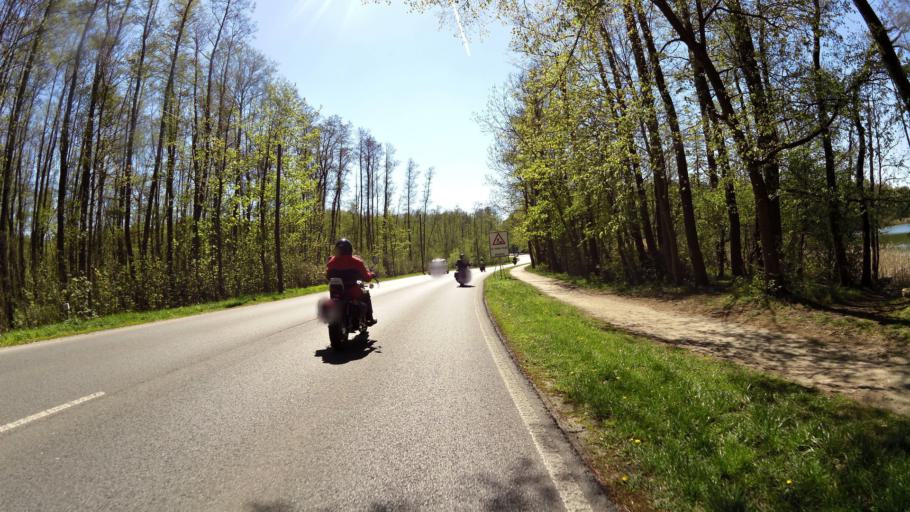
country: DE
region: Brandenburg
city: Strausberg
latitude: 52.5915
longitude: 13.8928
